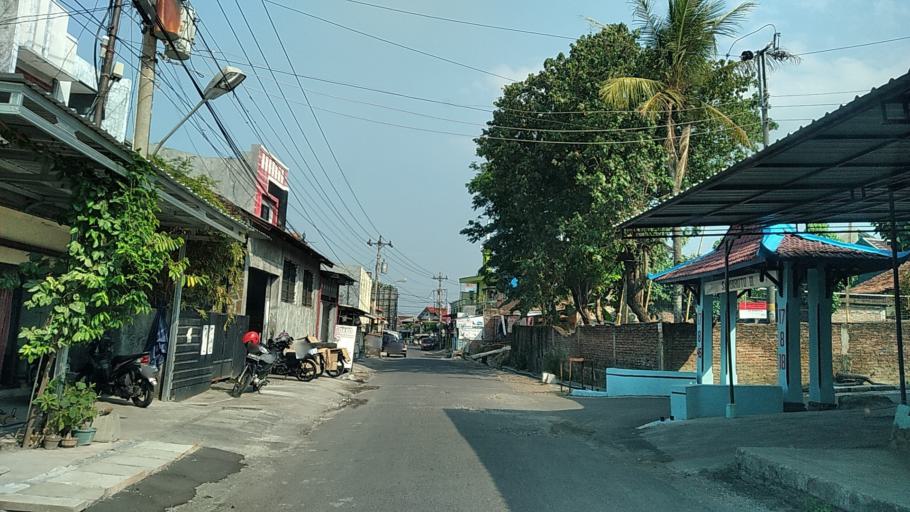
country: ID
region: Central Java
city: Semarang
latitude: -7.0240
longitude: 110.4589
